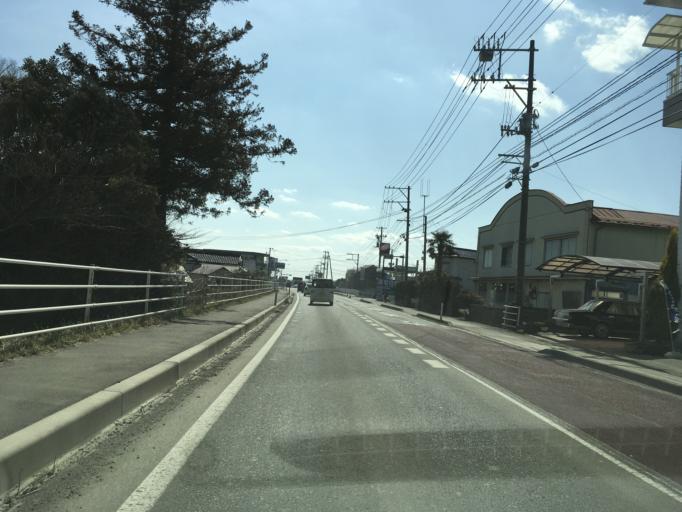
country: JP
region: Iwate
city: Ofunato
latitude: 38.8376
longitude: 141.5790
